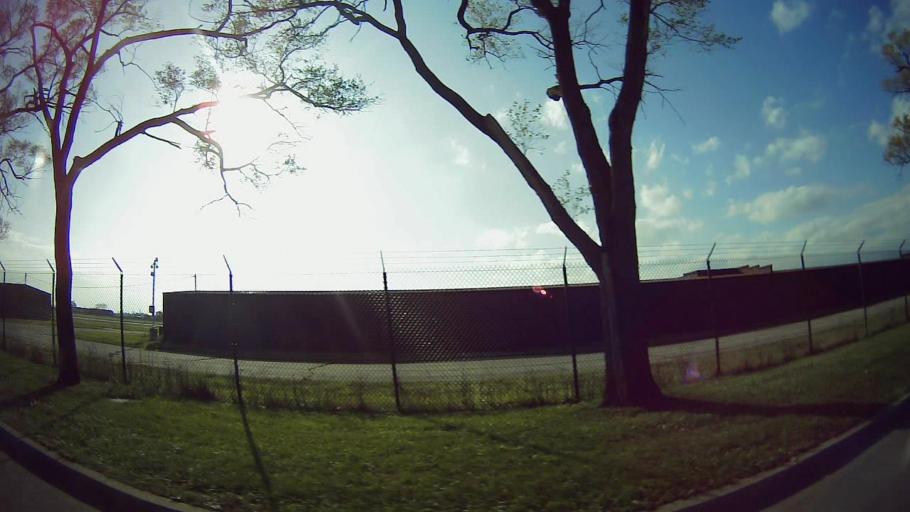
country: US
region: Michigan
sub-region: Wayne County
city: Hamtramck
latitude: 42.4146
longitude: -83.0090
